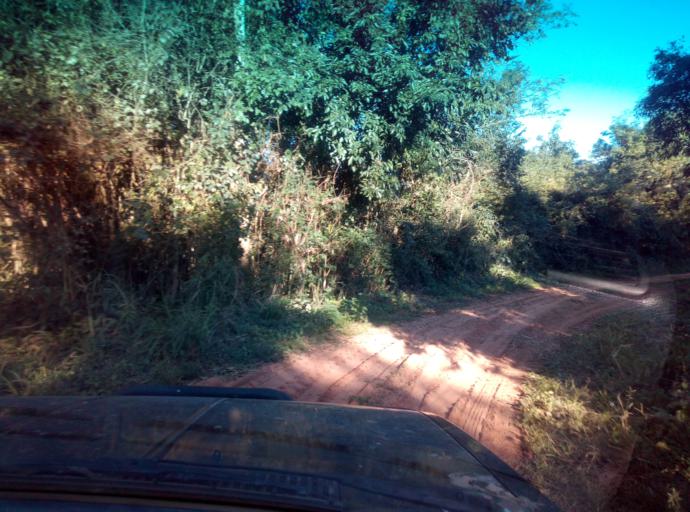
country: PY
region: Caaguazu
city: Carayao
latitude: -25.1826
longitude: -56.2624
